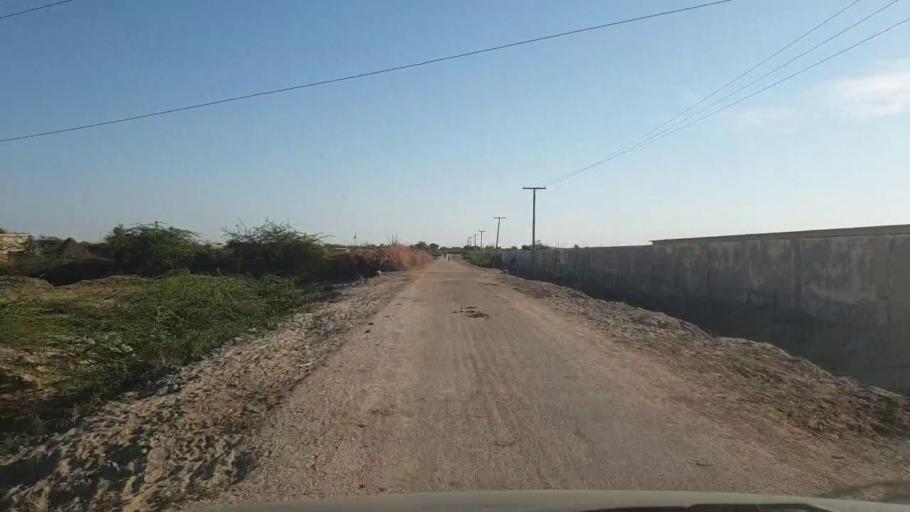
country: PK
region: Sindh
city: Dhoro Naro
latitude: 25.4279
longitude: 69.5438
